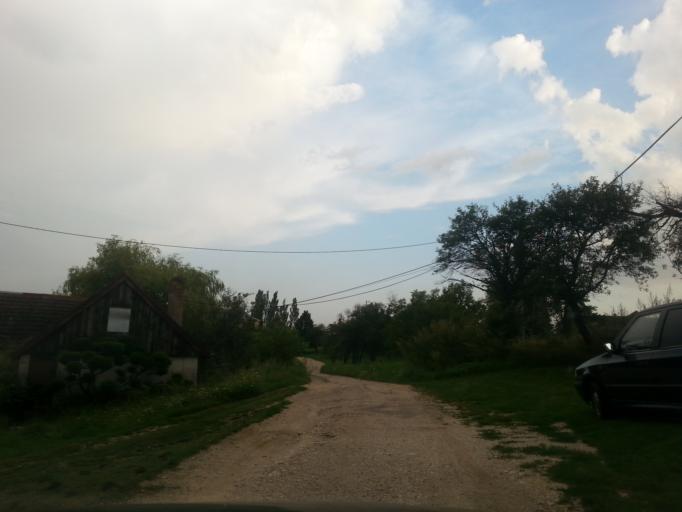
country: CZ
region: Zlin
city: Strani
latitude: 48.8379
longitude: 17.7496
